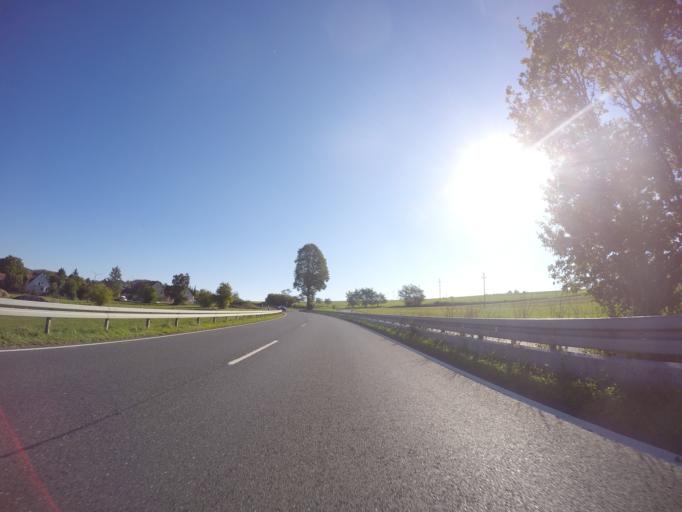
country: DE
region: Bavaria
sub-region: Regierungsbezirk Unterfranken
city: Remlingen
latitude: 49.8000
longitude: 9.6924
